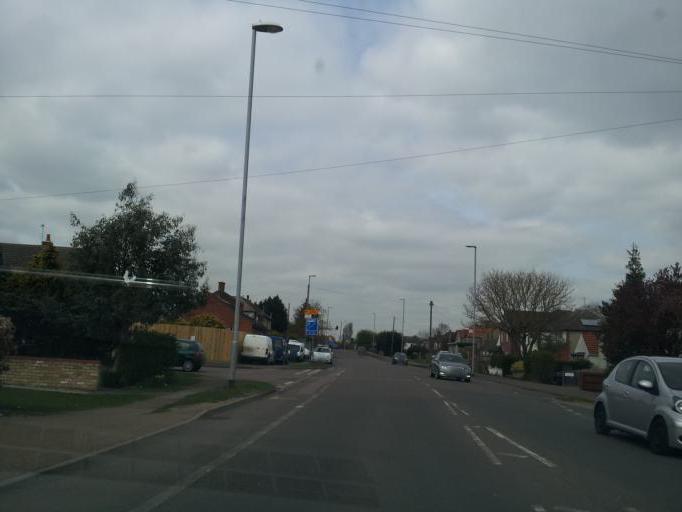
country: GB
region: England
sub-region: Cambridgeshire
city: Grantchester
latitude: 52.1678
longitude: 0.1171
